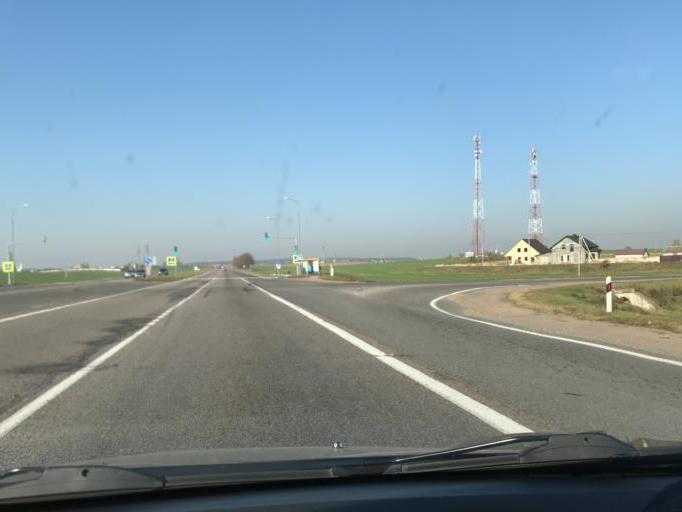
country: BY
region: Minsk
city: Luhavaya Slabada
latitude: 53.7345
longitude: 27.8491
